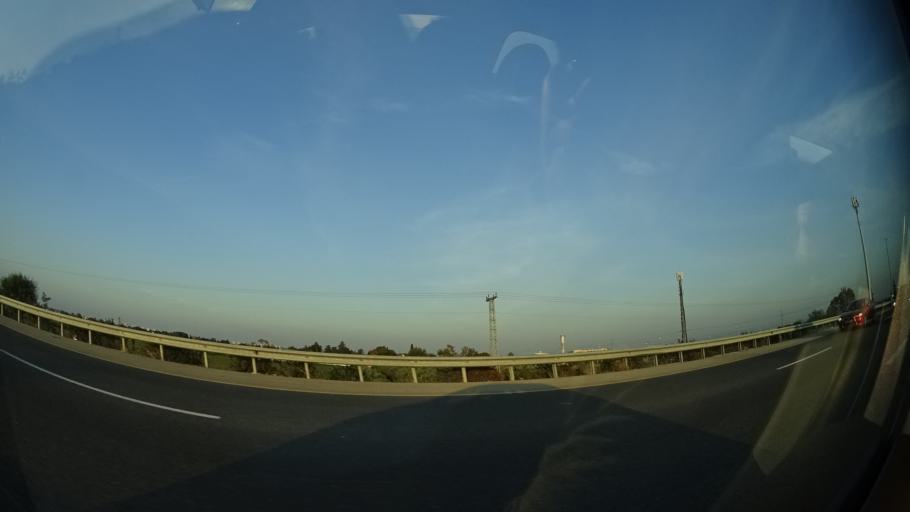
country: IL
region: Central District
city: Kefar Habad
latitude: 31.9964
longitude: 34.8534
